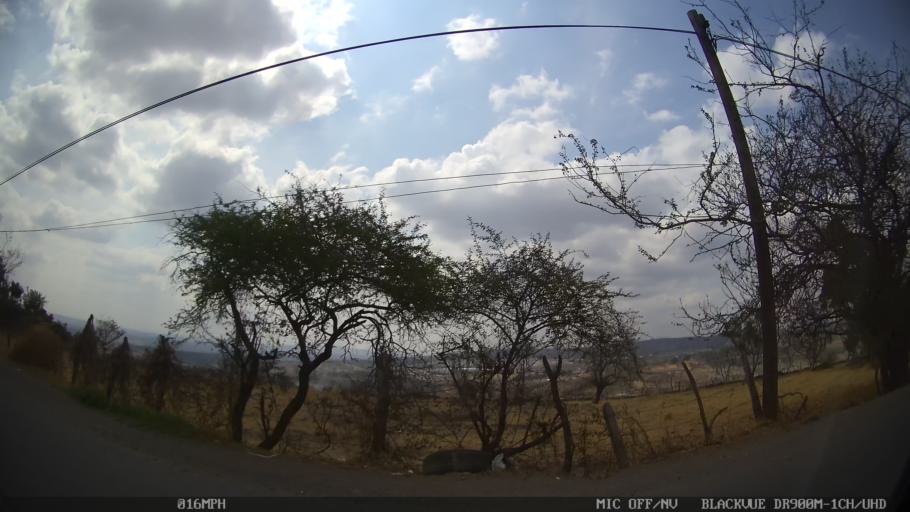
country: MX
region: Jalisco
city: Tonala
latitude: 20.6264
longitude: -103.2272
